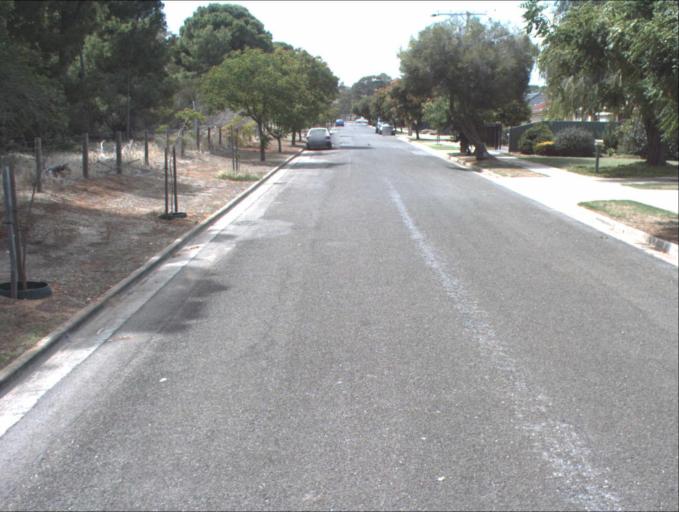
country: AU
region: South Australia
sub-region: Port Adelaide Enfield
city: Enfield
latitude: -34.8439
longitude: 138.6048
